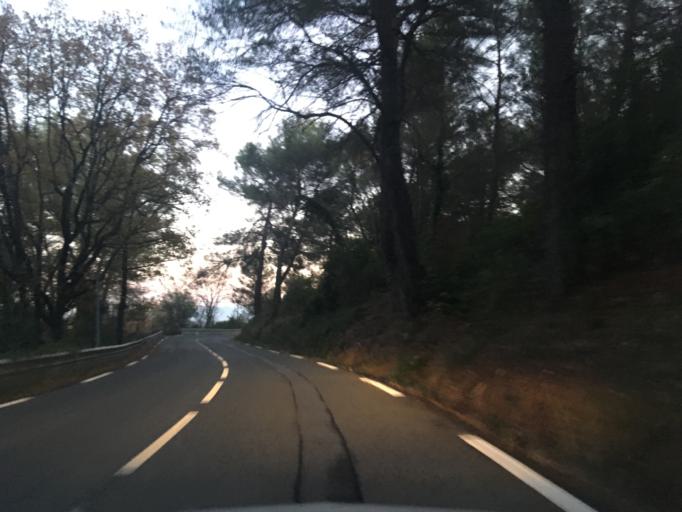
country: FR
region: Provence-Alpes-Cote d'Azur
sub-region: Departement du Var
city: Figanieres
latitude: 43.5355
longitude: 6.5028
